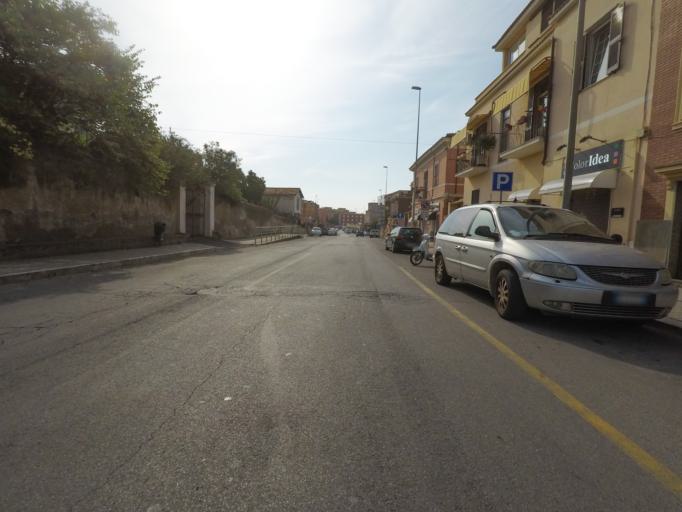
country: IT
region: Latium
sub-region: Citta metropolitana di Roma Capitale
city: Civitavecchia
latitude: 42.0974
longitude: 11.7967
